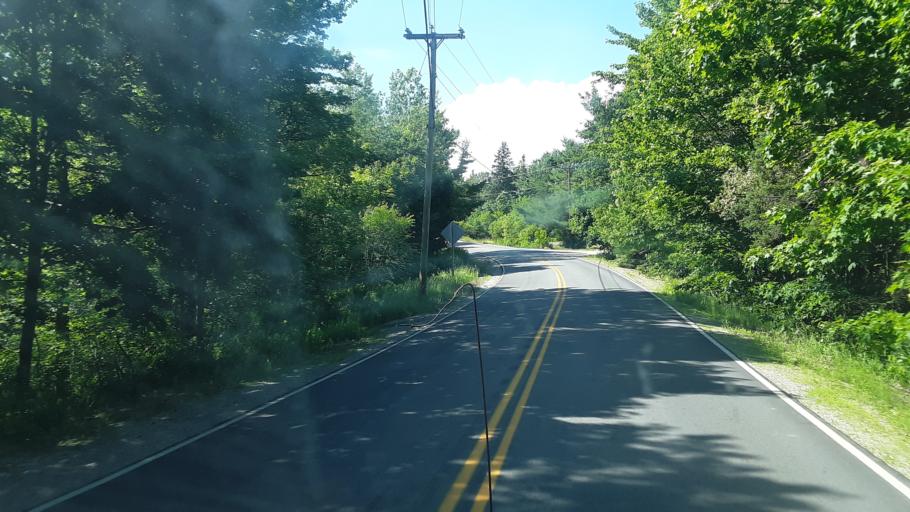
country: US
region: Maine
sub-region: Washington County
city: Cherryfield
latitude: 44.6164
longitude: -67.9254
